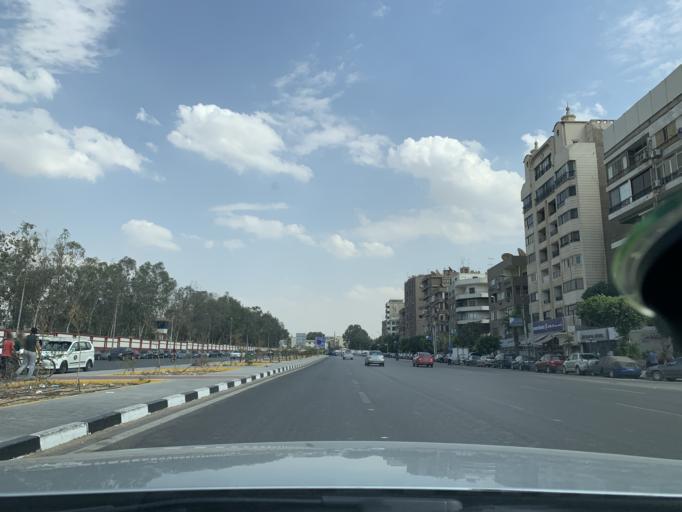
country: EG
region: Muhafazat al Qalyubiyah
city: Al Khankah
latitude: 30.1077
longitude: 31.3485
